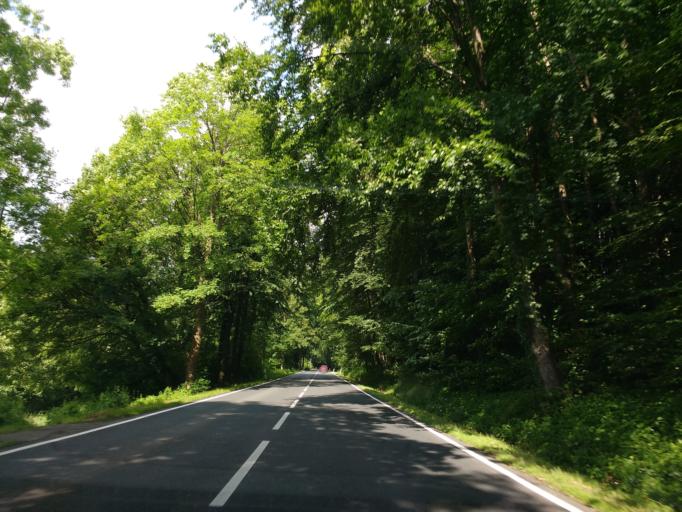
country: DE
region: North Rhine-Westphalia
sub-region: Regierungsbezirk Detmold
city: Lemgo
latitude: 52.0662
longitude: 8.9118
